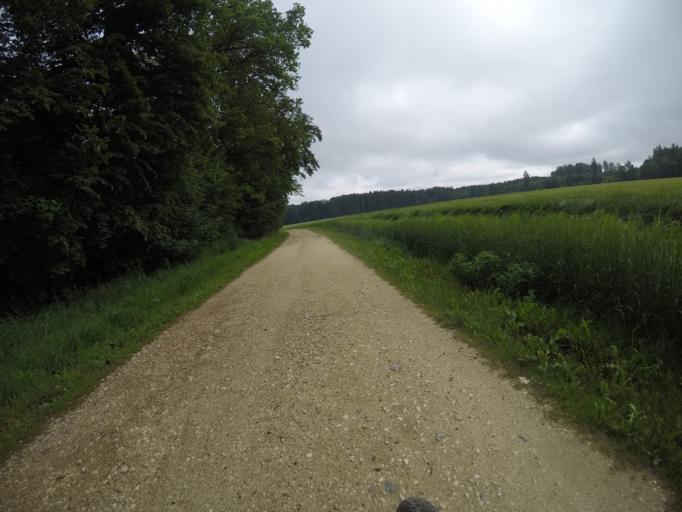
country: DE
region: Baden-Wuerttemberg
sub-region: Tuebingen Region
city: Dornstadt
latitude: 48.4787
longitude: 9.9575
